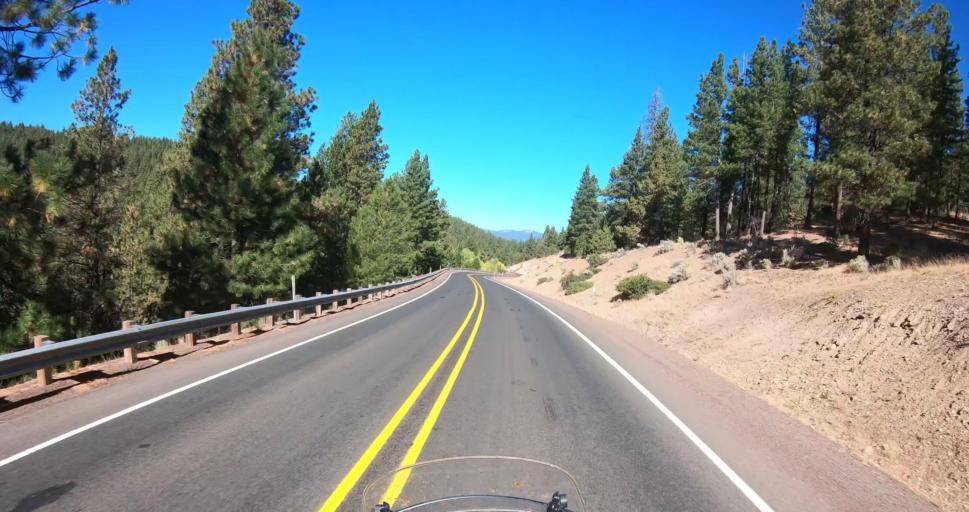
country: US
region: Oregon
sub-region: Lake County
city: Lakeview
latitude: 42.2524
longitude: -120.3285
